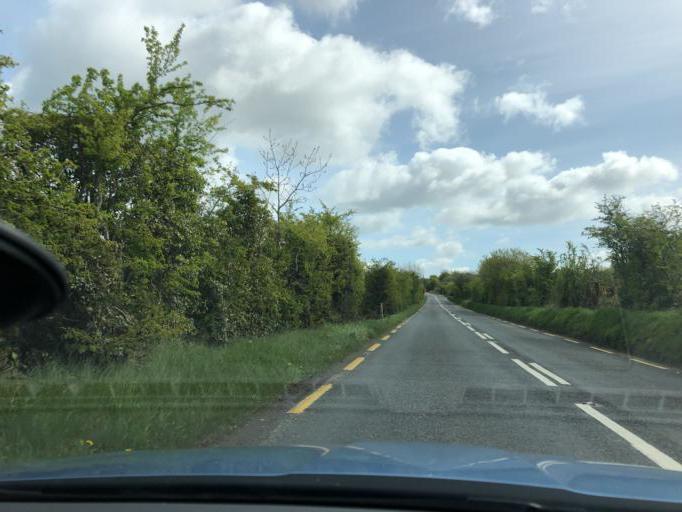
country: IE
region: Munster
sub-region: Ciarrai
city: Cill Airne
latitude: 52.0676
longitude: -9.3004
